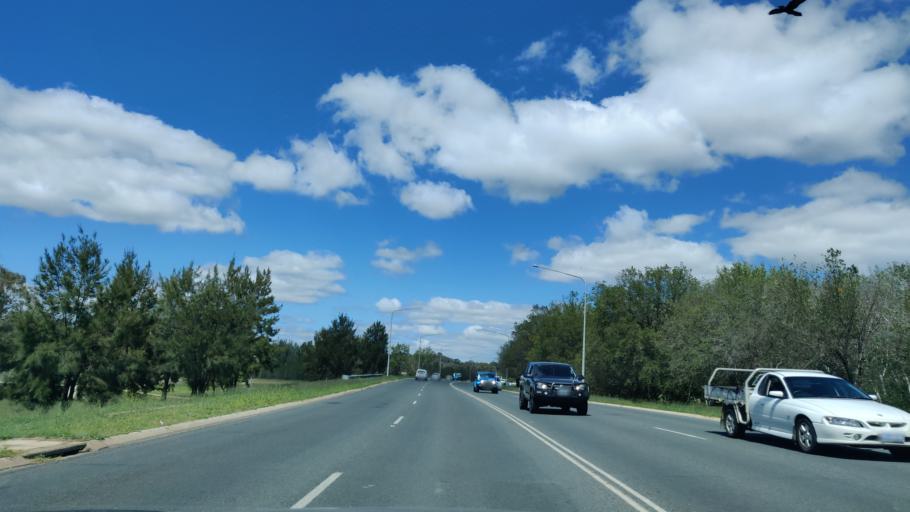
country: AU
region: Australian Capital Territory
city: Forrest
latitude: -35.3607
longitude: 149.0919
